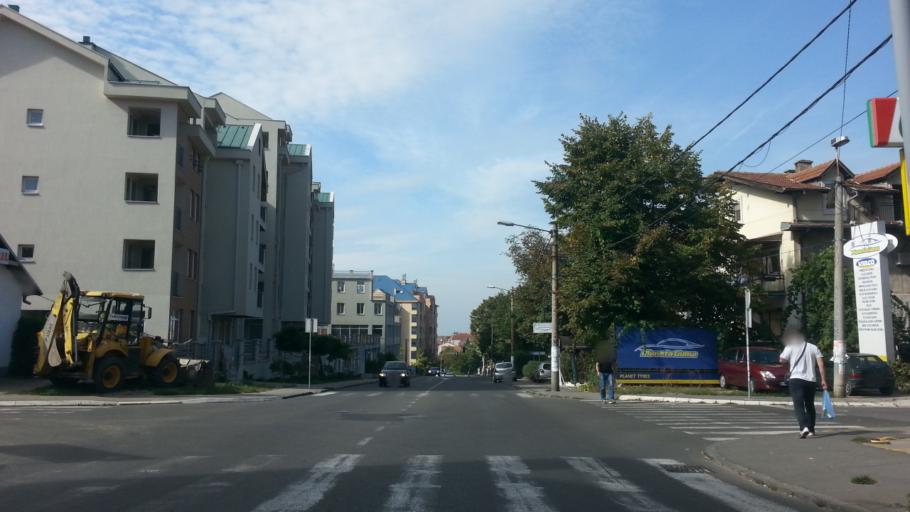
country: RS
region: Central Serbia
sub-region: Belgrade
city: Rakovica
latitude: 44.7509
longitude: 20.4269
